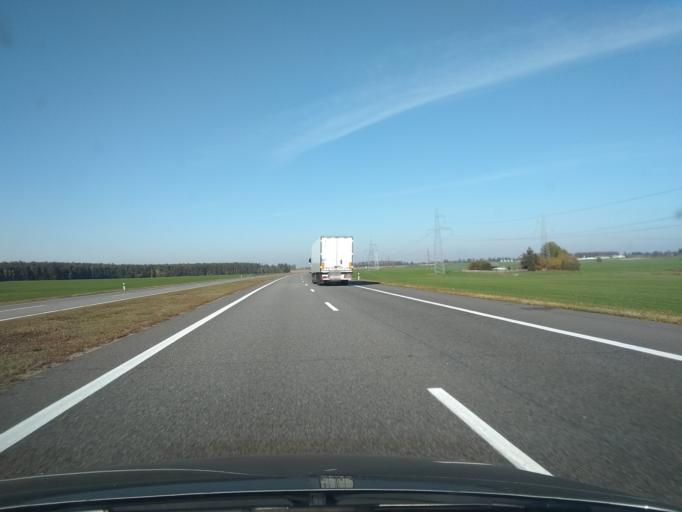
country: BY
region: Brest
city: Baranovichi
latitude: 53.0922
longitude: 25.8868
